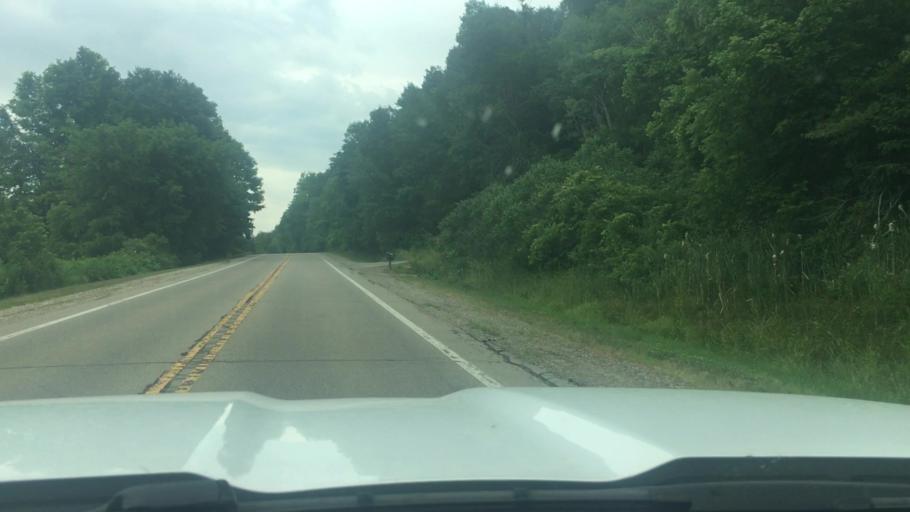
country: US
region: Michigan
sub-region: Ionia County
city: Saranac
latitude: 42.9634
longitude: -85.1530
